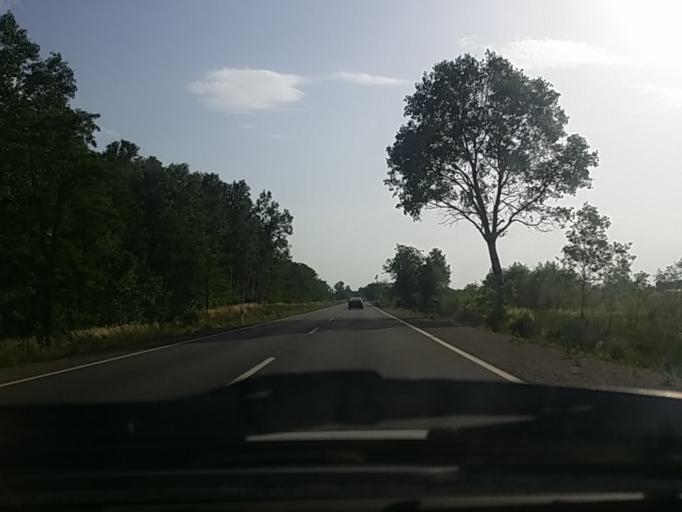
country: HU
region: Pest
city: Nagykata
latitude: 47.4526
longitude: 19.8283
